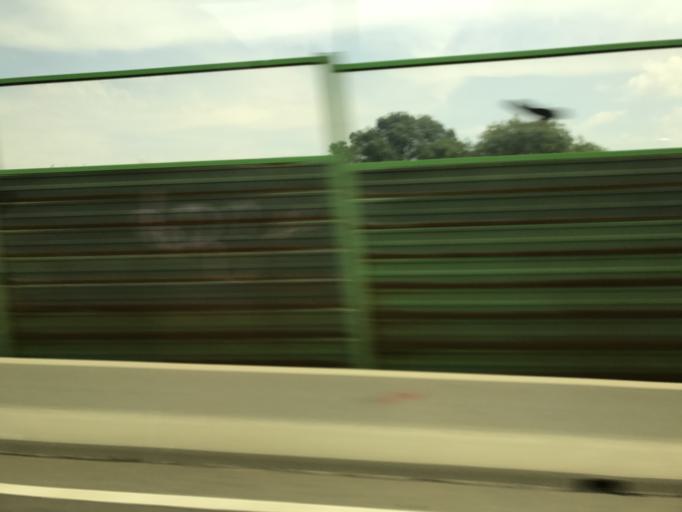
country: ES
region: Madrid
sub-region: Provincia de Madrid
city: La Cabrera
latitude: 40.9247
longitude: -3.6193
